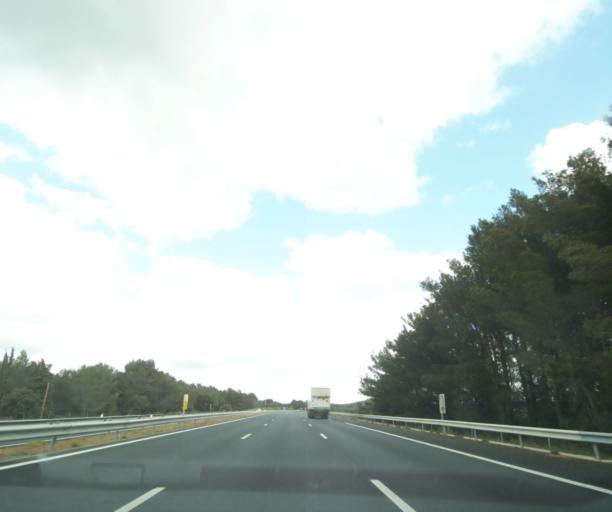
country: FR
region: Languedoc-Roussillon
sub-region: Departement du Gard
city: Ledenon
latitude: 43.8939
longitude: 4.5087
